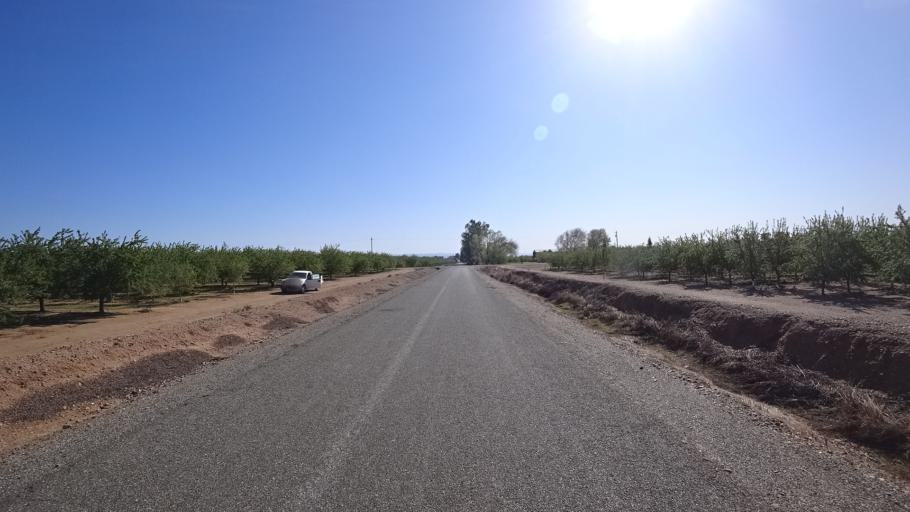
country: US
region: California
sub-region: Glenn County
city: Hamilton City
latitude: 39.7825
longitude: -122.0869
